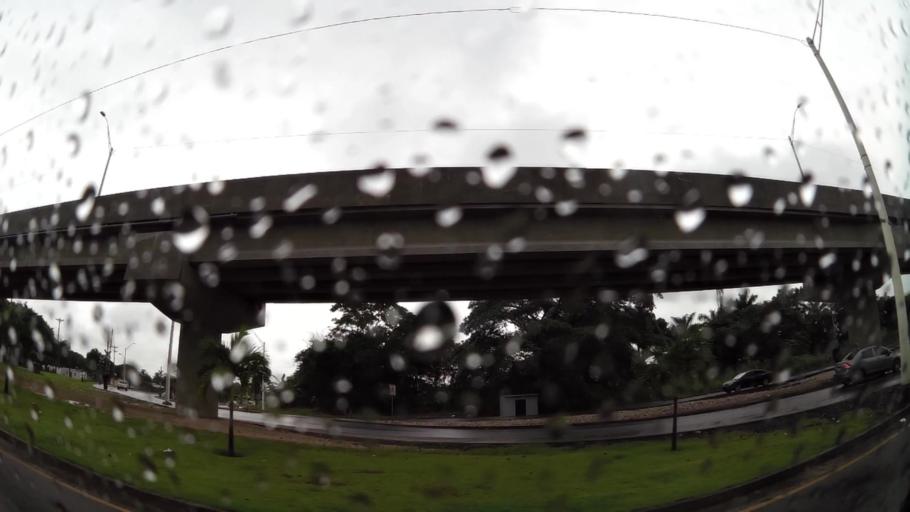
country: PA
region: Colon
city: Arco Iris
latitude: 9.3373
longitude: -79.8885
